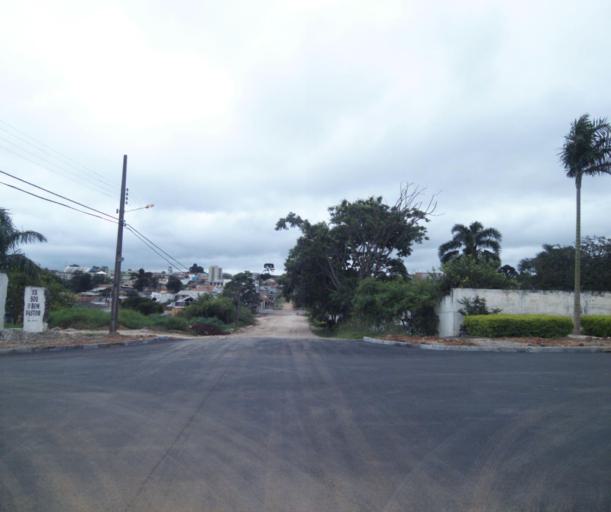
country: BR
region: Parana
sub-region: Quatro Barras
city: Quatro Barras
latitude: -25.3632
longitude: -49.1114
